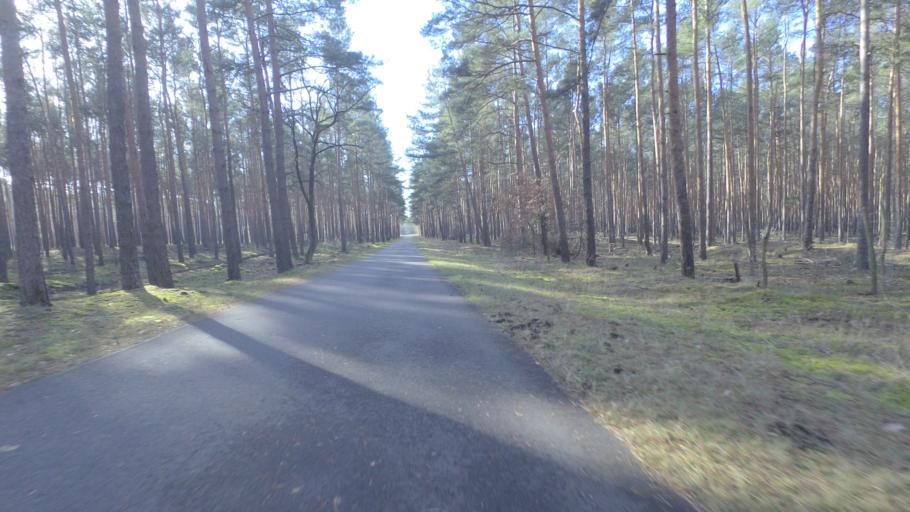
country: DE
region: Brandenburg
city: Luckenwalde
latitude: 52.0498
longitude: 13.1480
